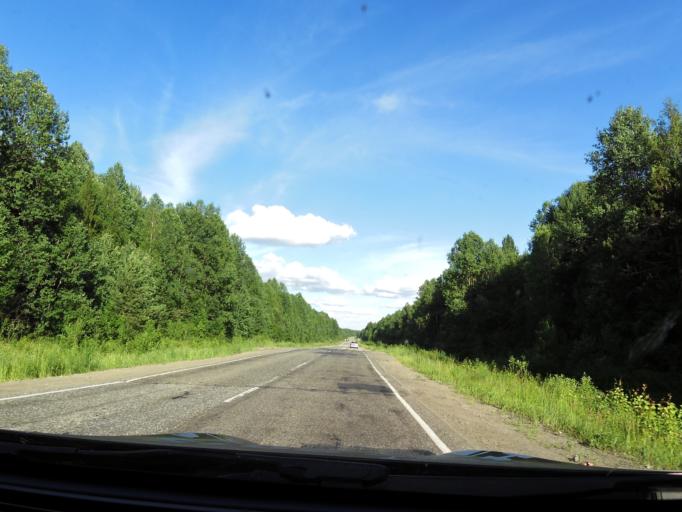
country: RU
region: Kirov
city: Omutninsk
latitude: 58.7579
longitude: 52.0244
